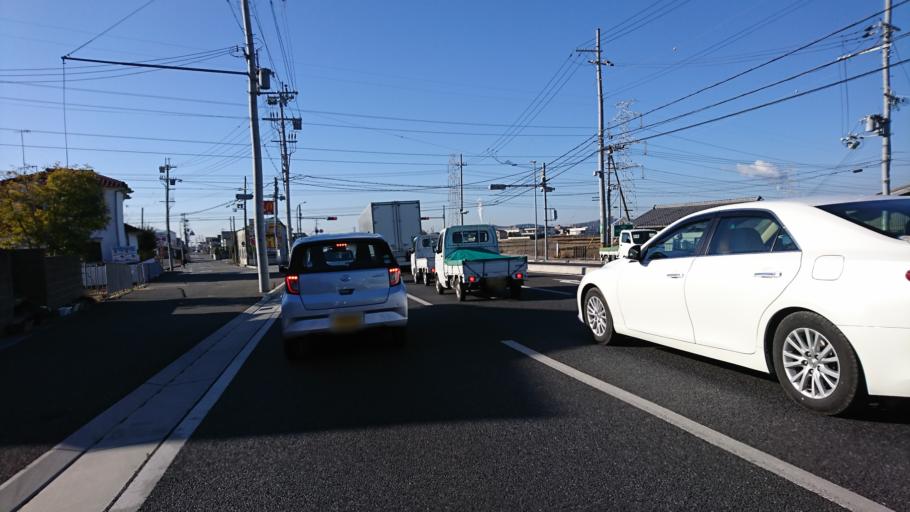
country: JP
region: Hyogo
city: Kakogawacho-honmachi
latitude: 34.8004
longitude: 134.8301
